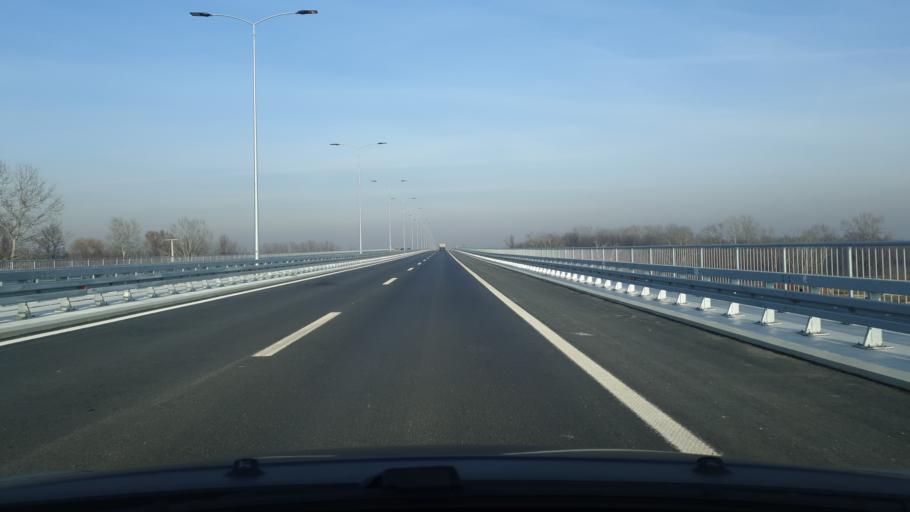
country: RS
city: Baric
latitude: 44.6597
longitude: 20.2397
